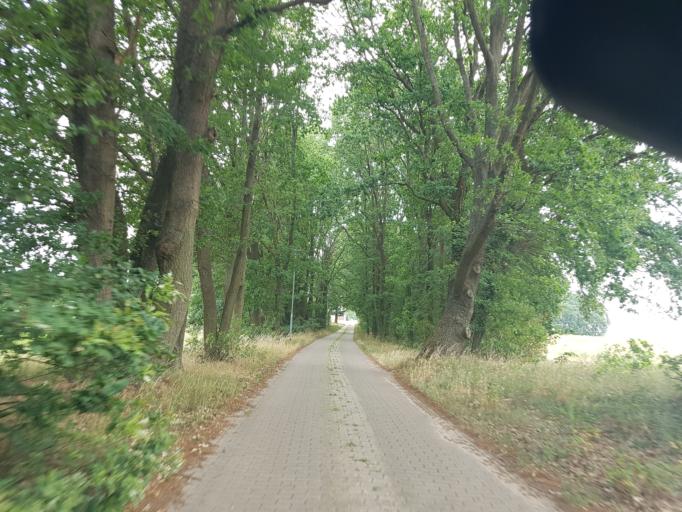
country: DE
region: Brandenburg
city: Treuenbrietzen
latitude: 52.0365
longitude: 12.8110
